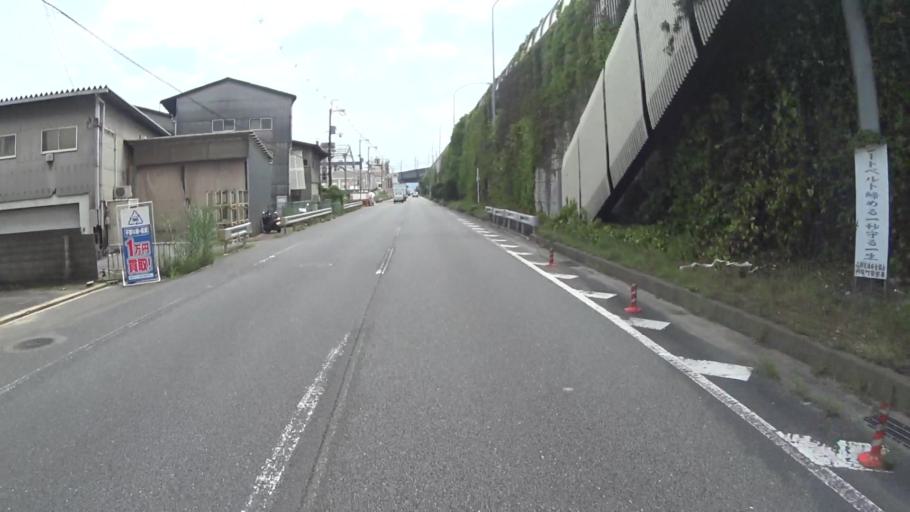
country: JP
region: Kyoto
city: Muko
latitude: 34.9352
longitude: 135.7155
